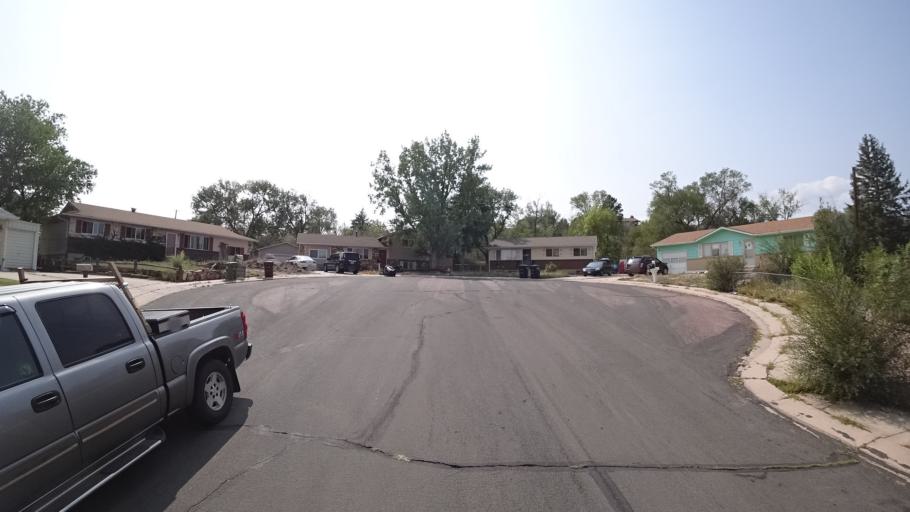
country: US
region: Colorado
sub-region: El Paso County
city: Stratmoor
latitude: 38.7990
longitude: -104.7697
